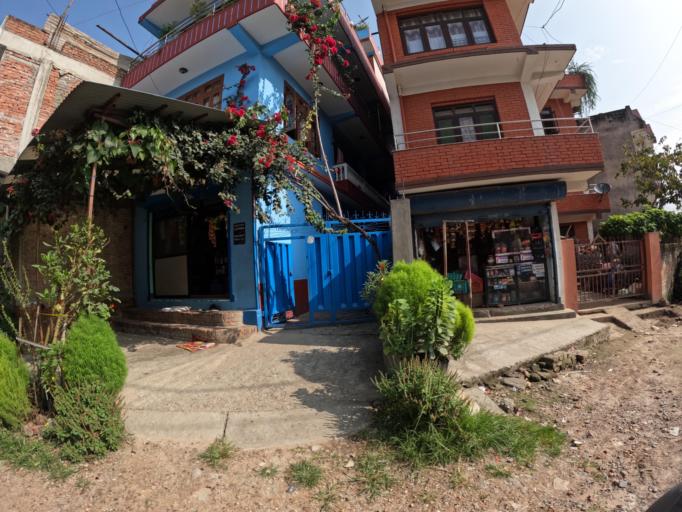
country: NP
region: Central Region
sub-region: Bagmati Zone
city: Bhaktapur
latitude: 27.6804
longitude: 85.4461
